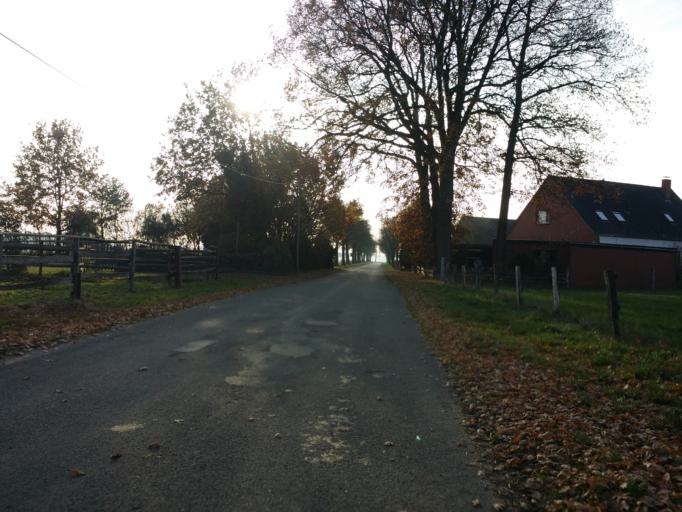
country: DE
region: Lower Saxony
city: Reessum
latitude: 53.1305
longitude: 9.1986
